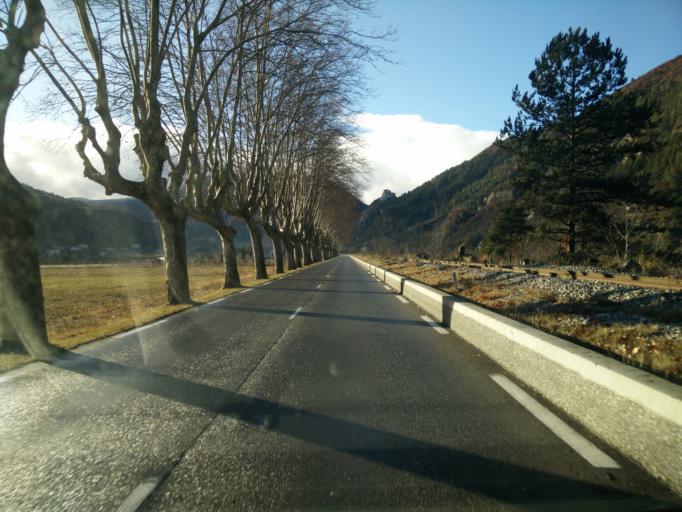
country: FR
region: Provence-Alpes-Cote d'Azur
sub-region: Departement des Alpes-Maritimes
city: Puget-Theniers
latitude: 43.9520
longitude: 6.8343
